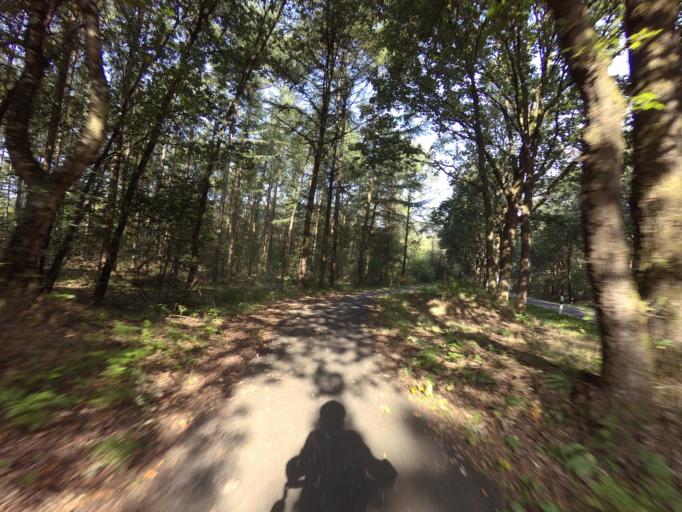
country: DE
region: Lower Saxony
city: Wielen
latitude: 52.5417
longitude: 6.6992
